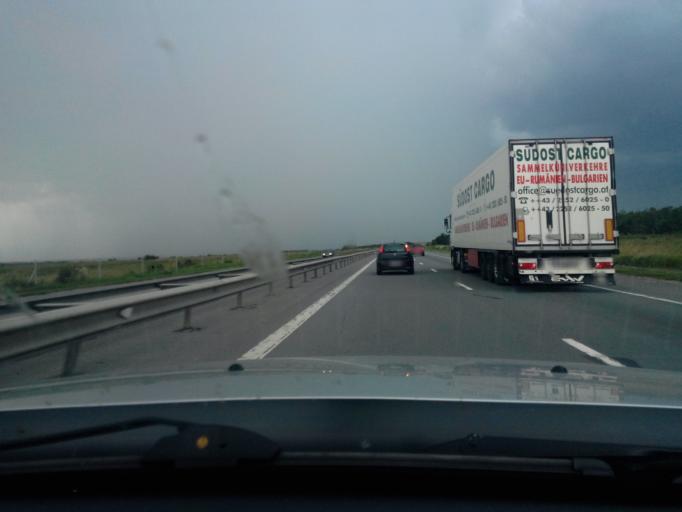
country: RO
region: Arges
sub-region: Comuna Ratesti
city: Ratesti
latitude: 44.7303
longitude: 25.1192
